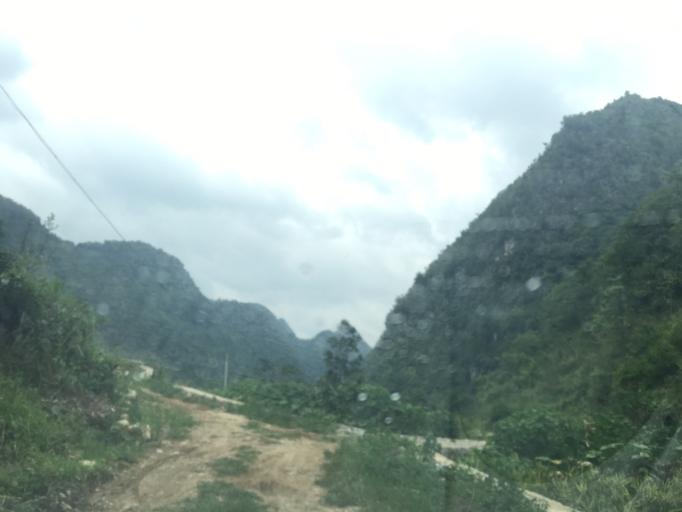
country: CN
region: Guangxi Zhuangzu Zizhiqu
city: Xinzhou
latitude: 25.2186
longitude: 105.6282
